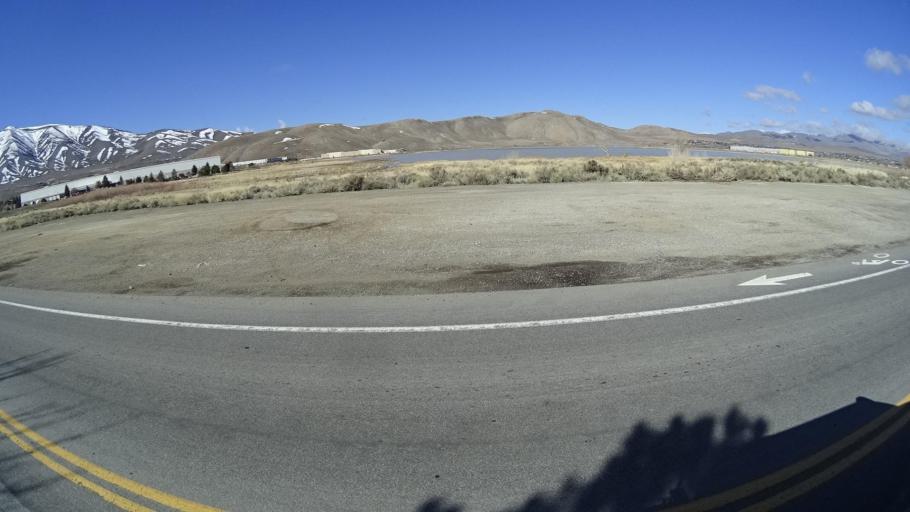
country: US
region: Nevada
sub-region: Washoe County
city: Lemmon Valley
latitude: 39.6383
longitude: -119.8970
